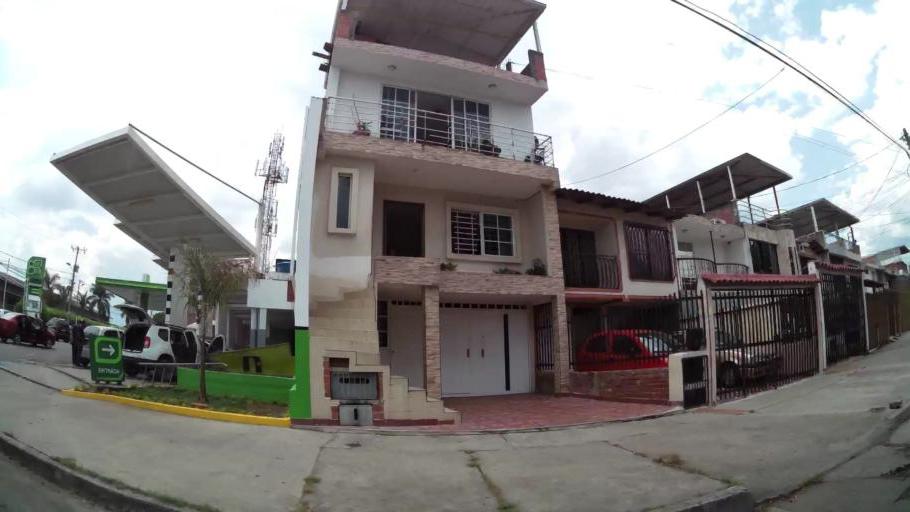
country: CO
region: Valle del Cauca
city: Cali
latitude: 3.4660
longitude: -76.4909
